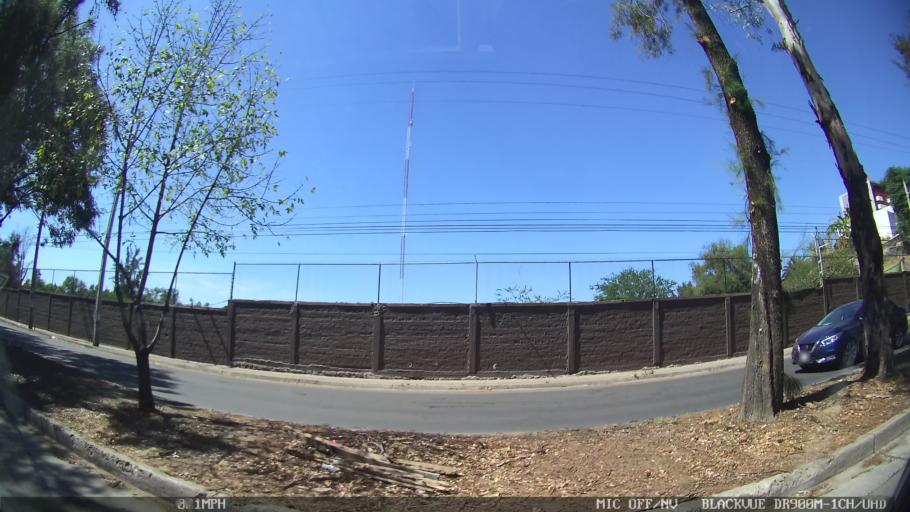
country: MX
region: Jalisco
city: Tlaquepaque
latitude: 20.6494
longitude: -103.2978
